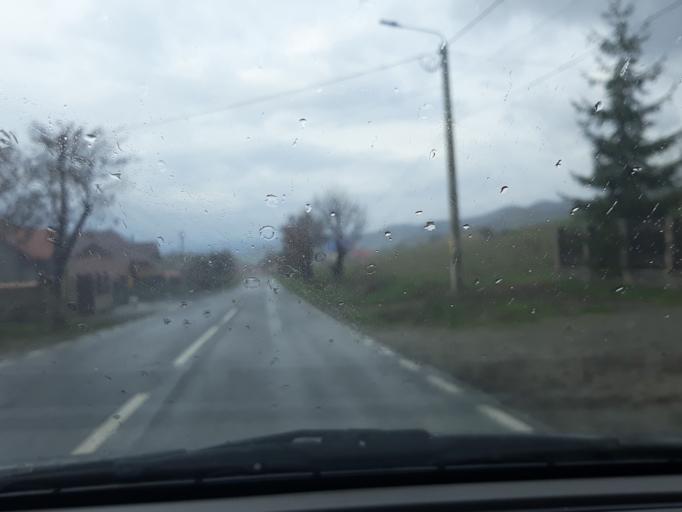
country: RO
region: Harghita
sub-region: Comuna Corund
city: Corund
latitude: 46.4825
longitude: 25.1716
